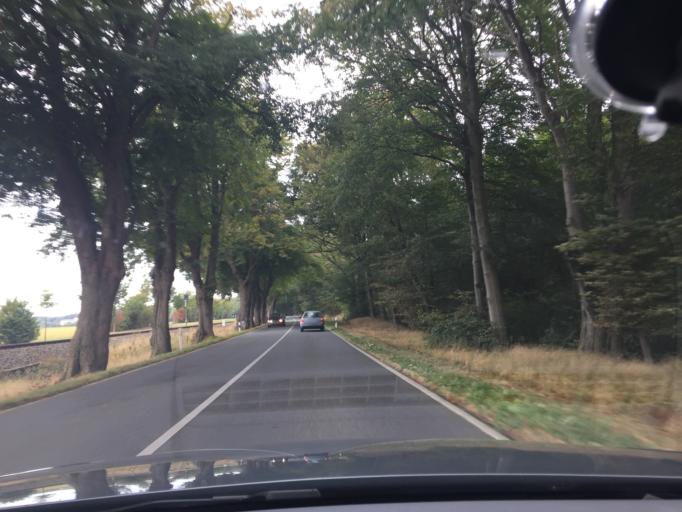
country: DE
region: Mecklenburg-Vorpommern
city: Bad Doberan
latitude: 54.1339
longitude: 11.8582
